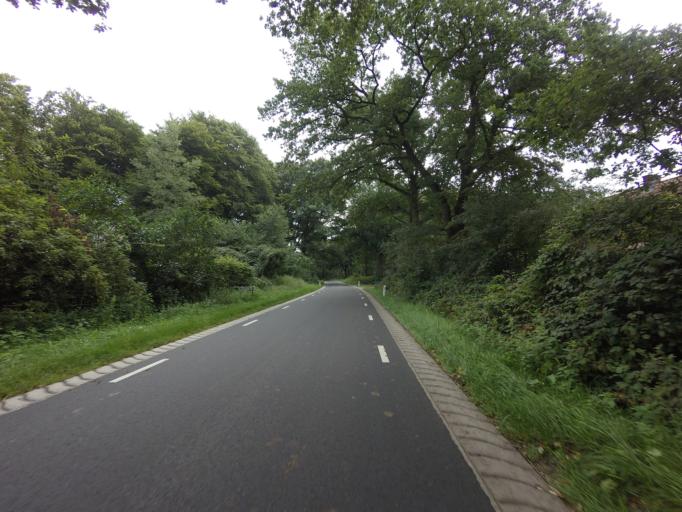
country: NL
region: Gelderland
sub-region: Gemeente Barneveld
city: Terschuur
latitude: 52.1208
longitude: 5.4902
